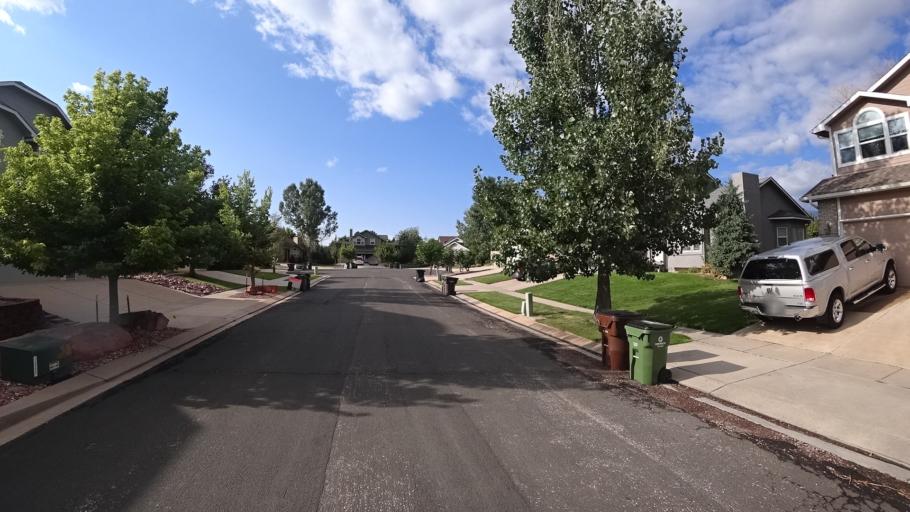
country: US
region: Colorado
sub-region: El Paso County
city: Manitou Springs
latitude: 38.9099
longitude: -104.8618
